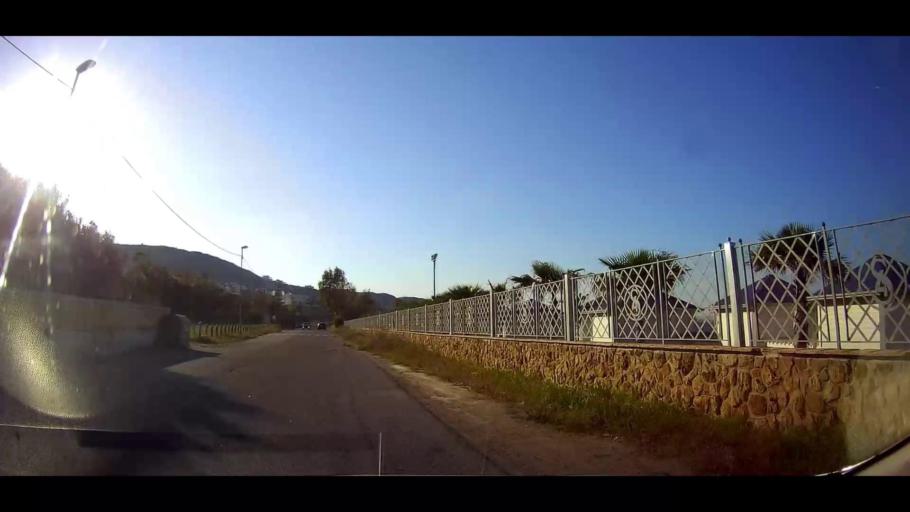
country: IT
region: Calabria
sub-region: Provincia di Crotone
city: Crotone
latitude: 39.0498
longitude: 17.1430
